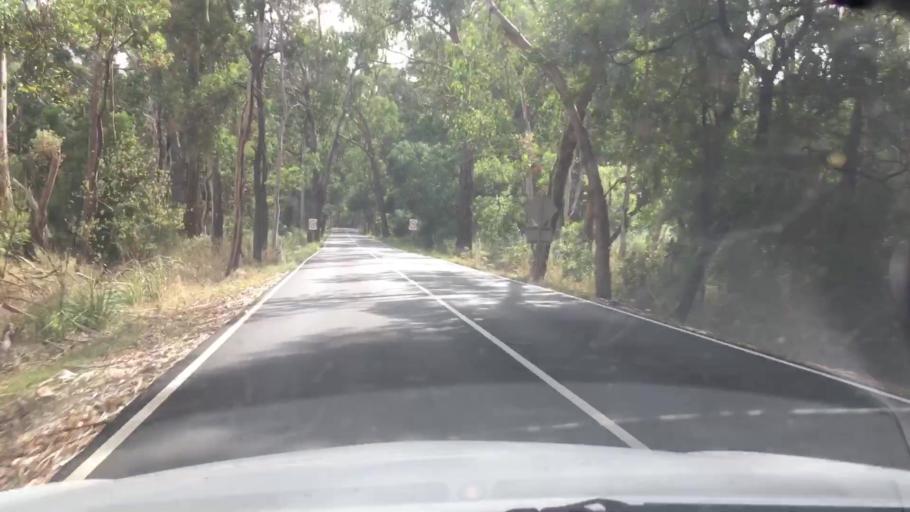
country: AU
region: Victoria
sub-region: Yarra Ranges
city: Woori Yallock
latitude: -37.8145
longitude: 145.5016
